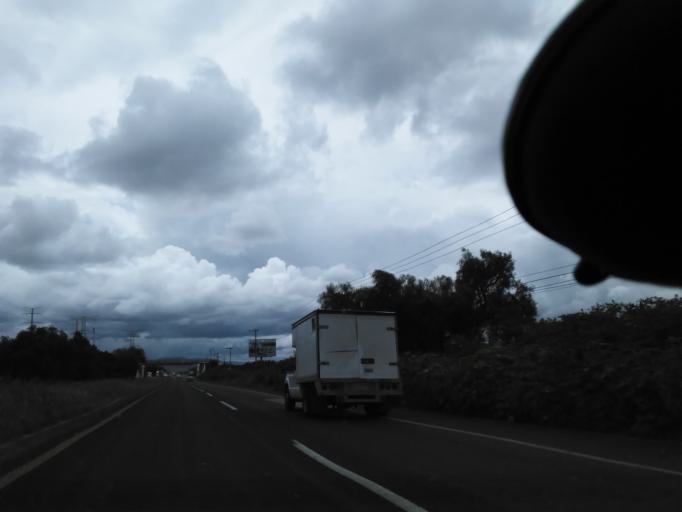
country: MX
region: Hidalgo
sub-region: Tula de Allende
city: Residencial Arboledas
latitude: 20.0609
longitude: -99.2826
